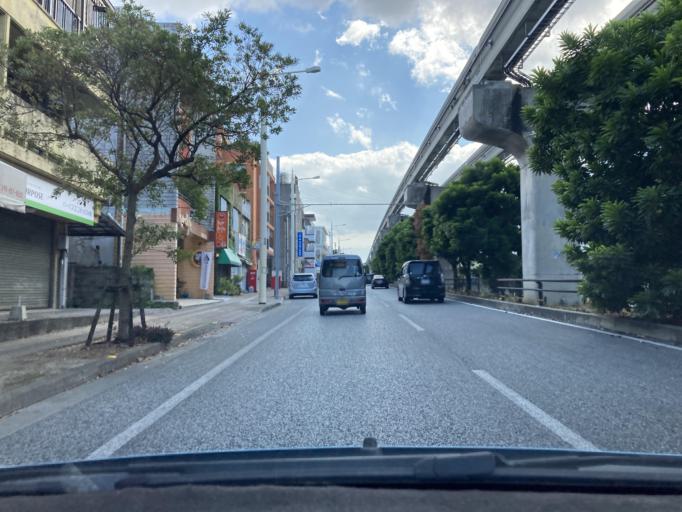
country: JP
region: Okinawa
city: Naha-shi
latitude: 26.2210
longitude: 127.7222
